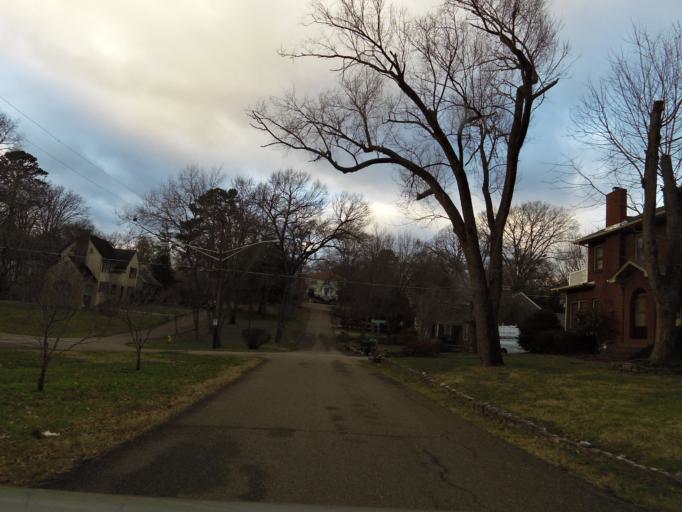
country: US
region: Tennessee
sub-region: Knox County
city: Knoxville
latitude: 36.0057
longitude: -83.9002
